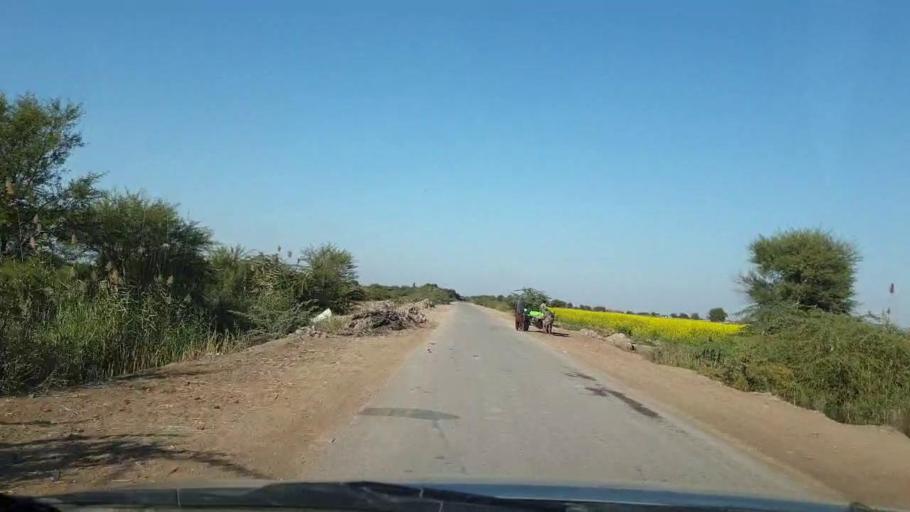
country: PK
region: Sindh
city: Jhol
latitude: 25.8238
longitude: 68.9481
